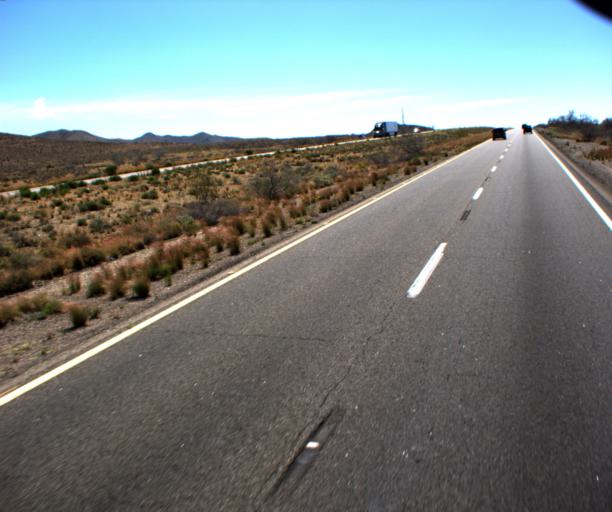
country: US
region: Arizona
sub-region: Mohave County
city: Dolan Springs
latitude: 35.4492
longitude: -114.2970
